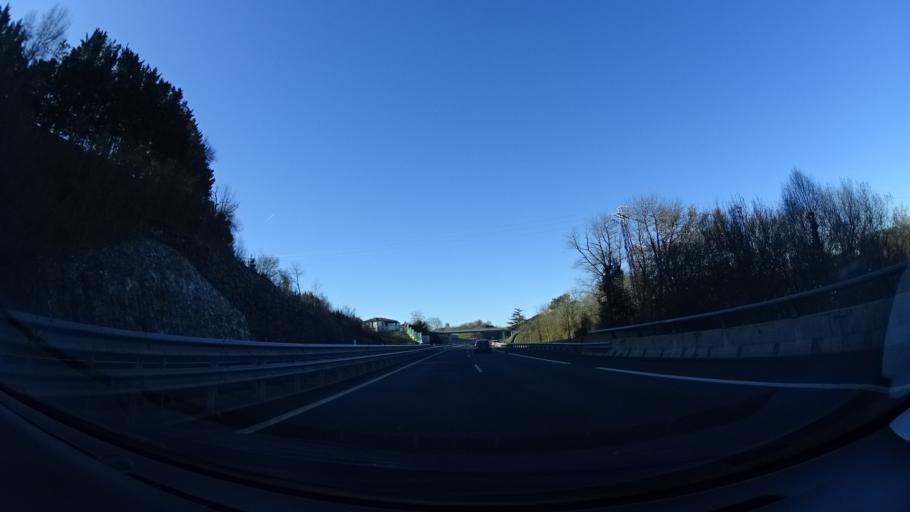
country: ES
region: Basque Country
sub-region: Provincia de Guipuzcoa
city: Hernani
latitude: 43.2766
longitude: -1.9980
